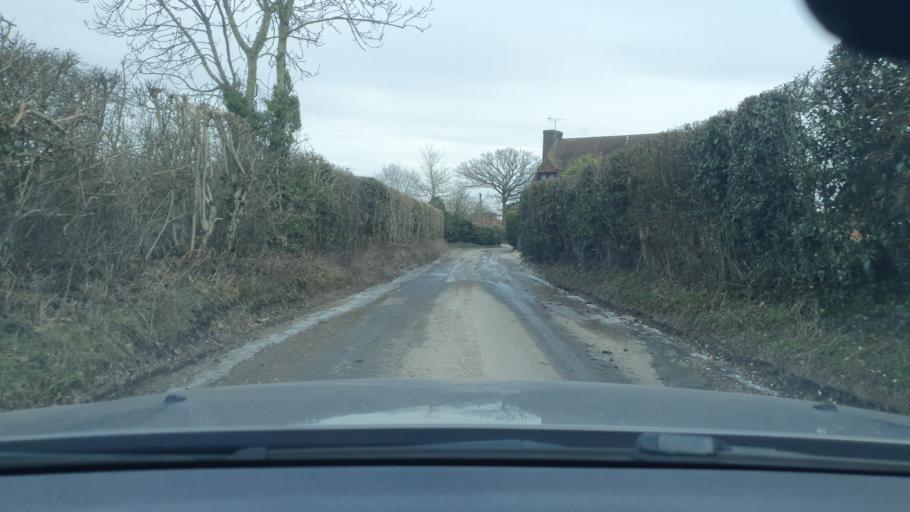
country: GB
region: England
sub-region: West Berkshire
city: Kintbury
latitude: 51.3718
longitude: -1.4601
